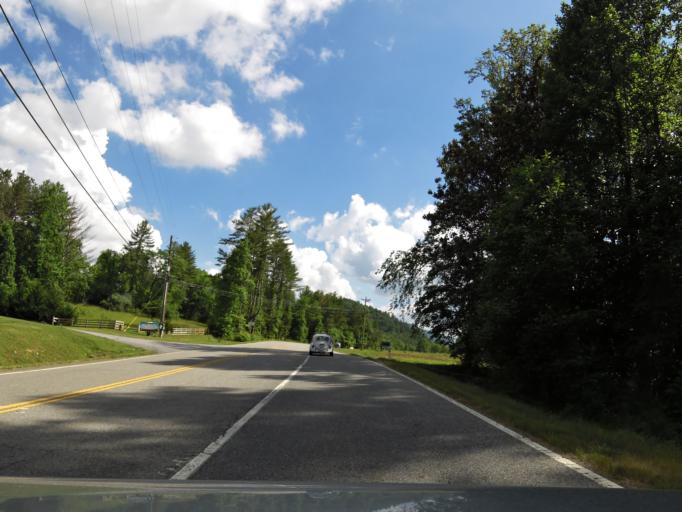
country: US
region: Georgia
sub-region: Towns County
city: Hiawassee
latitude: 34.8568
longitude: -83.7225
